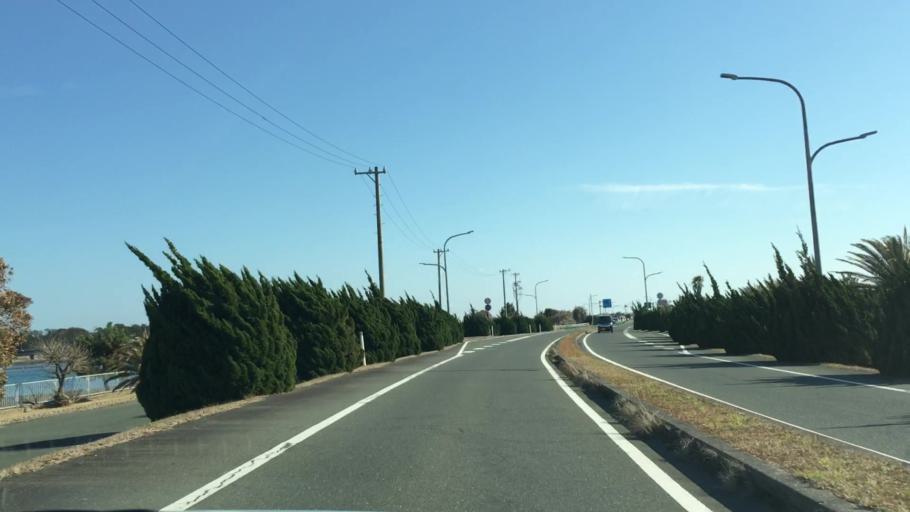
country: JP
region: Shizuoka
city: Kosai-shi
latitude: 34.7069
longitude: 137.6100
